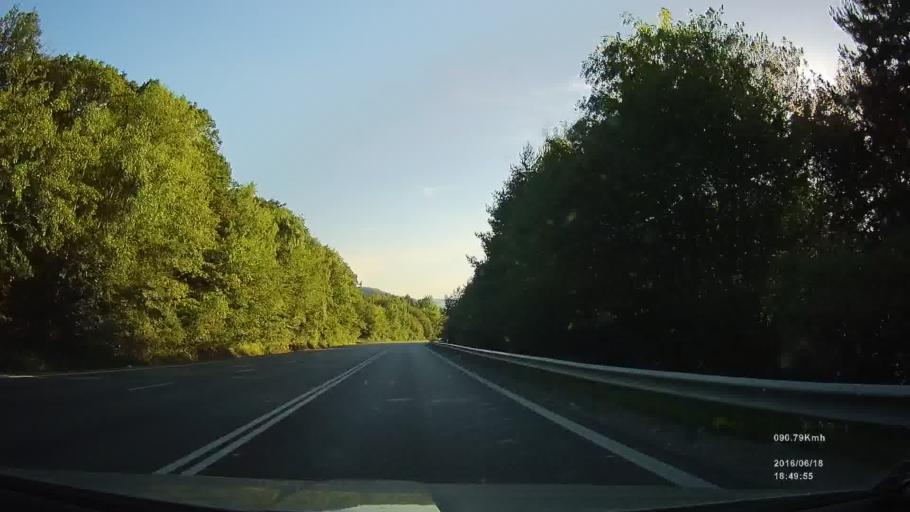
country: SK
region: Kosicky
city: Secovce
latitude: 48.7410
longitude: 21.5194
